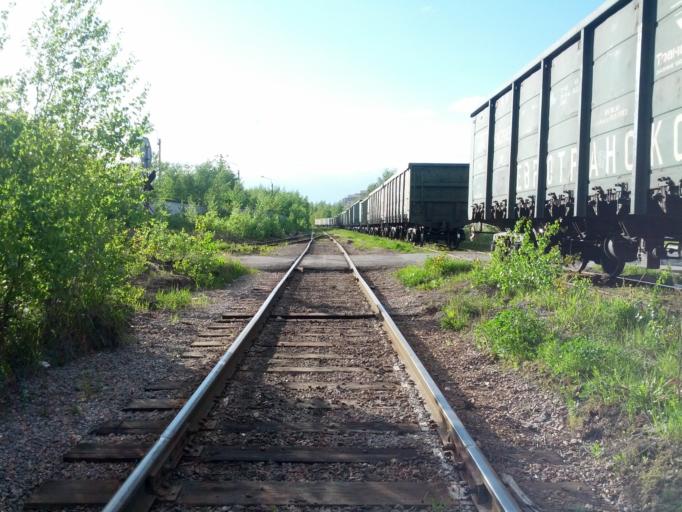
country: RU
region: St.-Petersburg
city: Obukhovo
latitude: 59.9093
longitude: 30.4442
